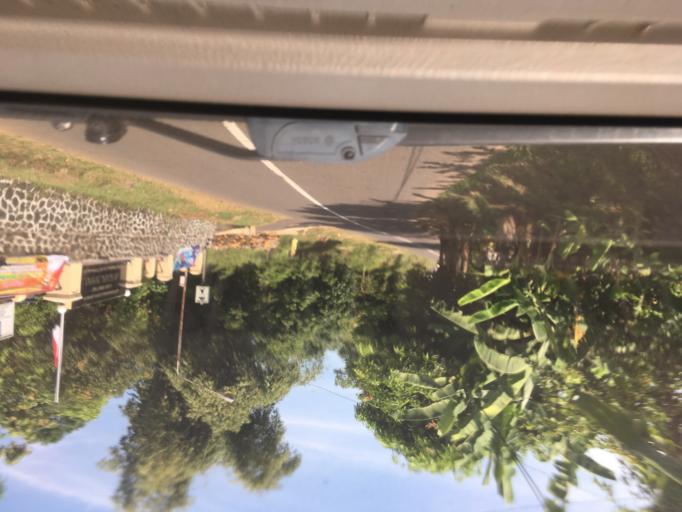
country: ID
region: West Java
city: Cilengkrang
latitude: -6.9565
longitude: 108.0950
